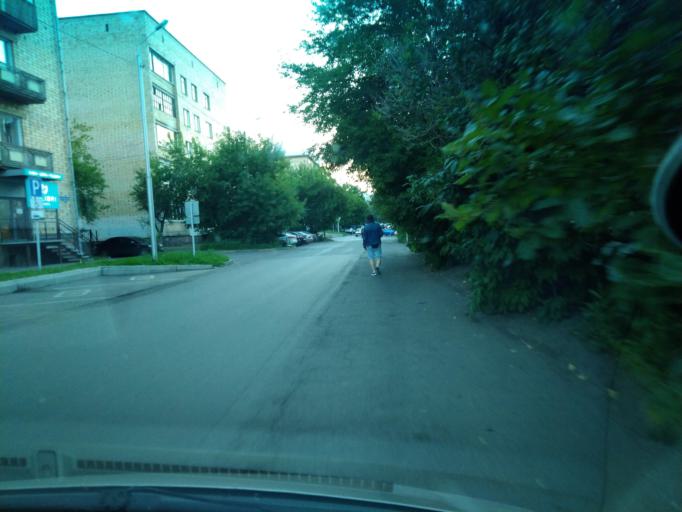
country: RU
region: Krasnoyarskiy
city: Krasnoyarsk
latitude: 56.0135
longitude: 92.8495
